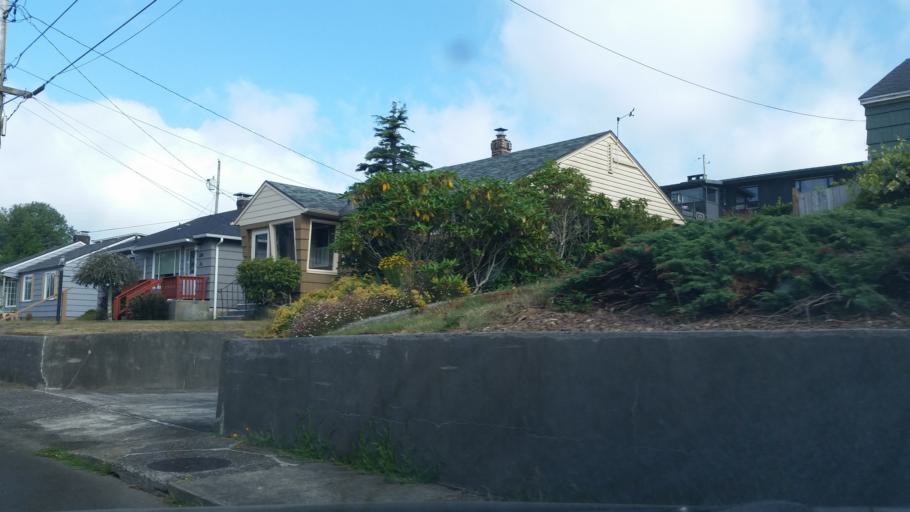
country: US
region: Oregon
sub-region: Clatsop County
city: Astoria
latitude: 46.1833
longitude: -123.8519
